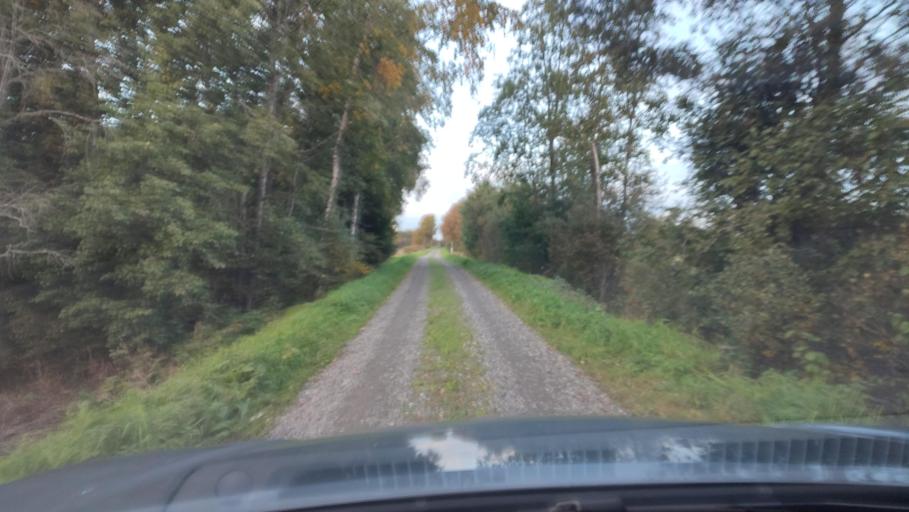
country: FI
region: Ostrobothnia
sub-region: Sydosterbotten
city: Kristinestad
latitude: 62.2352
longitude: 21.4513
